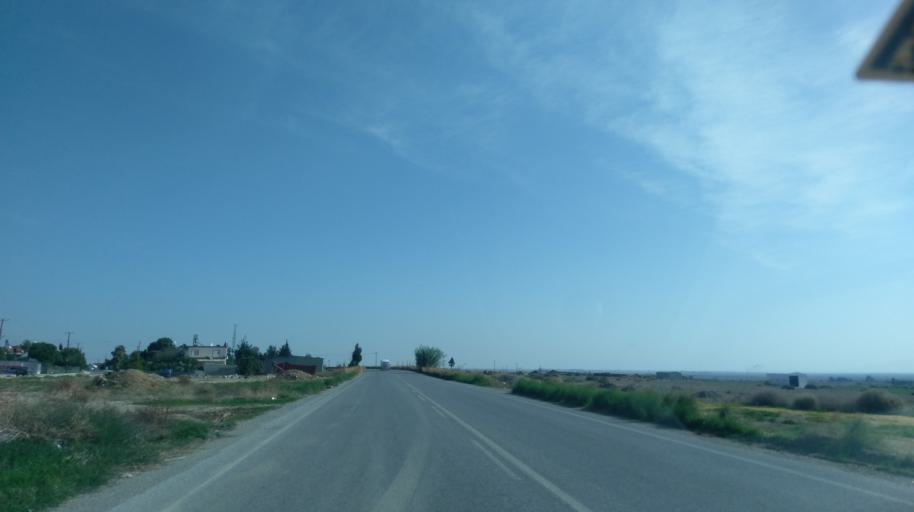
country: CY
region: Ammochostos
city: Lefkonoiko
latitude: 35.2423
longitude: 33.5985
